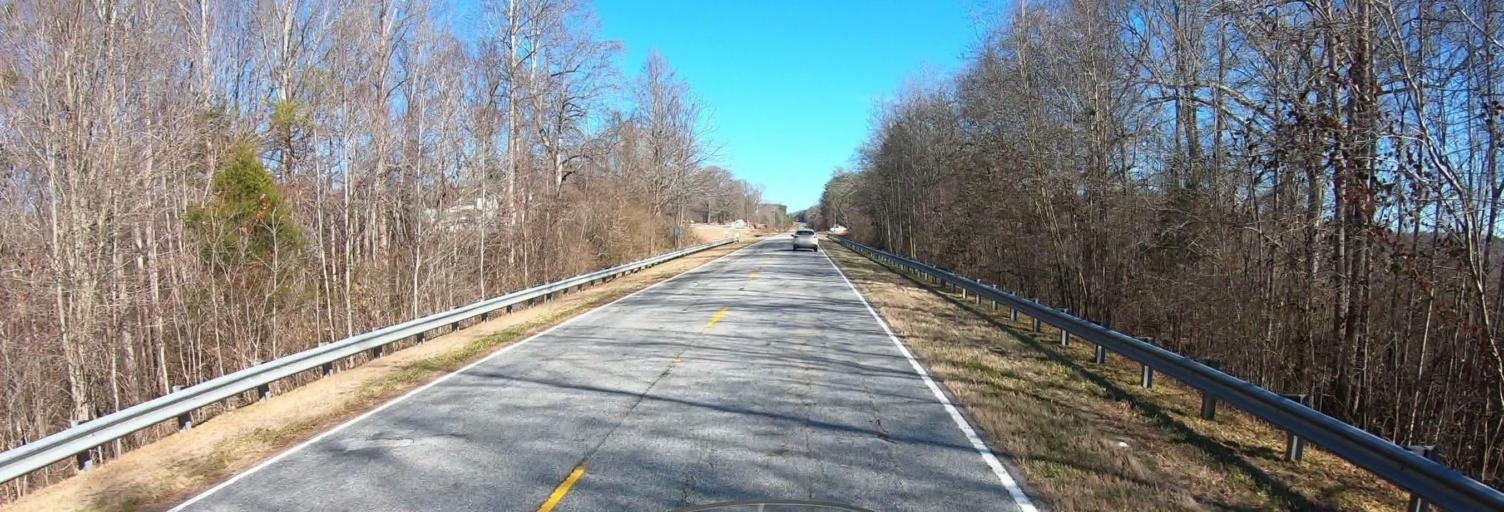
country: US
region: South Carolina
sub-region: Oconee County
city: Westminster
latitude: 34.6121
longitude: -83.1978
